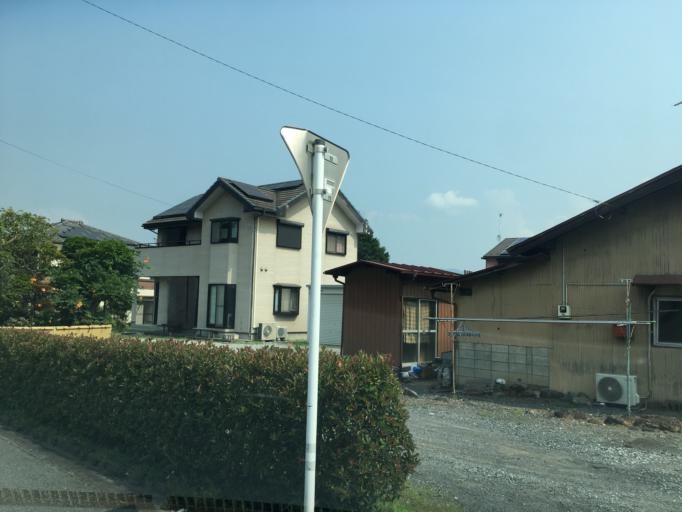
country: JP
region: Saitama
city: Chichibu
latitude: 36.0074
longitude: 139.1108
